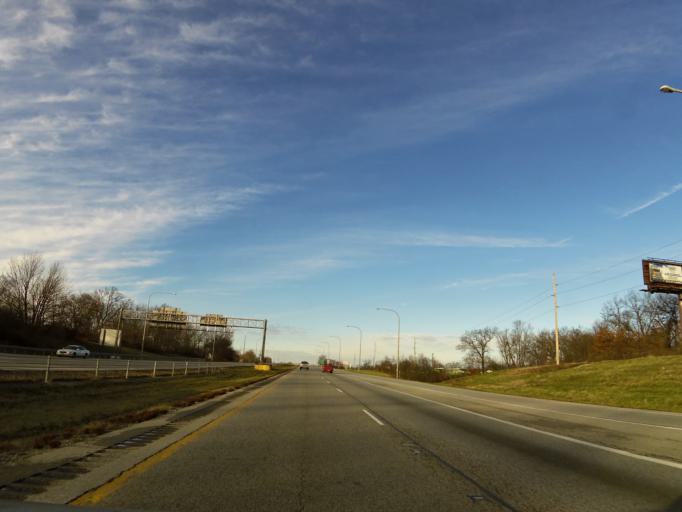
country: US
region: Illinois
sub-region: Vermilion County
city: Tilton
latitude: 40.1051
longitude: -87.6405
